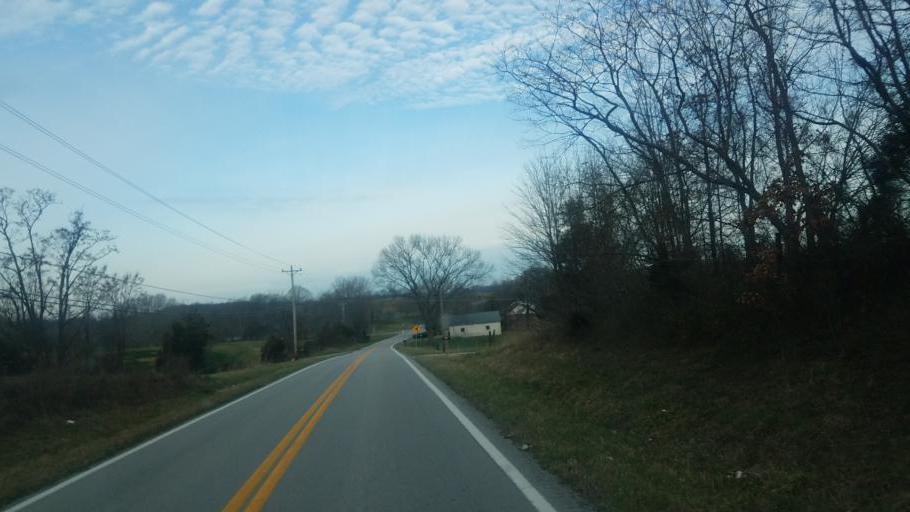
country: US
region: Kentucky
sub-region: Clinton County
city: Albany
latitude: 36.7653
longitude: -85.1655
